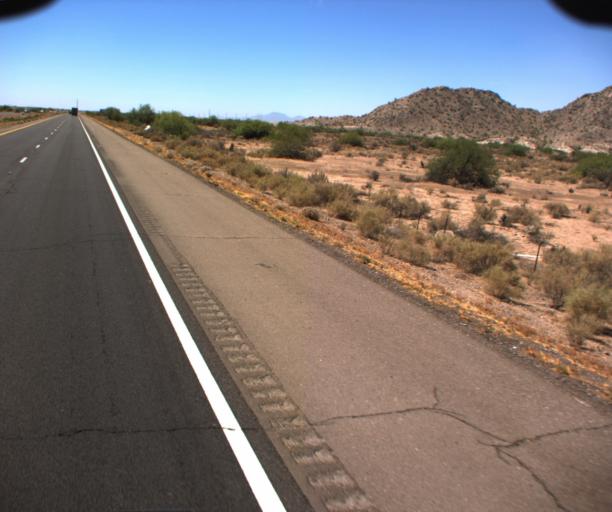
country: US
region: Arizona
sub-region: Pinal County
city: Maricopa
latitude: 33.1568
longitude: -112.0079
